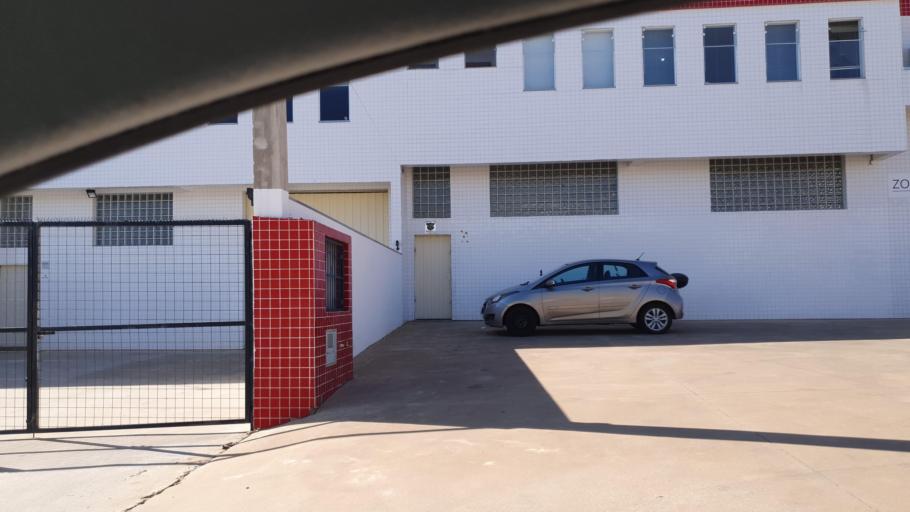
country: BR
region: Sao Paulo
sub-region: Sorocaba
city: Sorocaba
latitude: -23.4452
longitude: -47.4408
